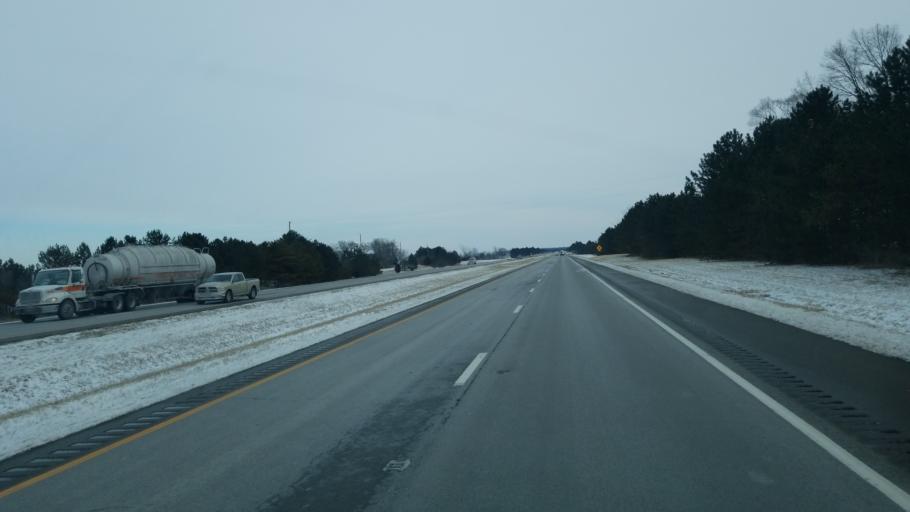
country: US
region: Ohio
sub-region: Wyandot County
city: Carey
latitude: 40.9583
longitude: -83.4523
